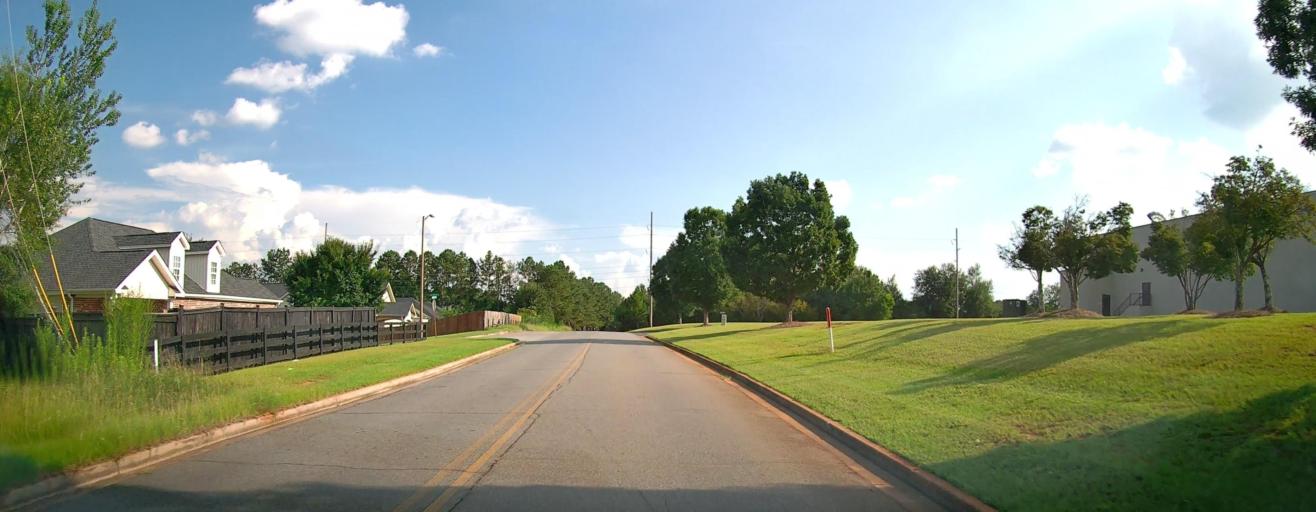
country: US
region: Georgia
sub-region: Houston County
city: Warner Robins
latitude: 32.5918
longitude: -83.6274
